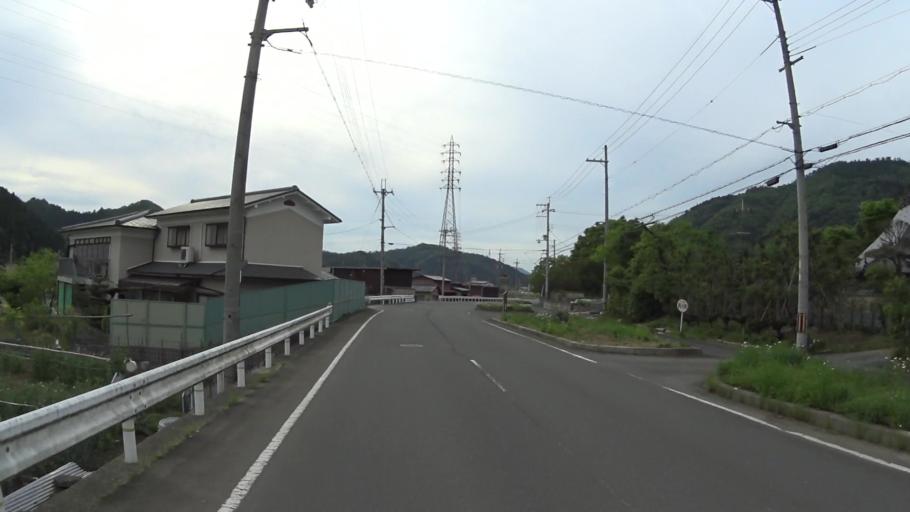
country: JP
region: Kyoto
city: Kameoka
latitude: 35.1033
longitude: 135.5292
